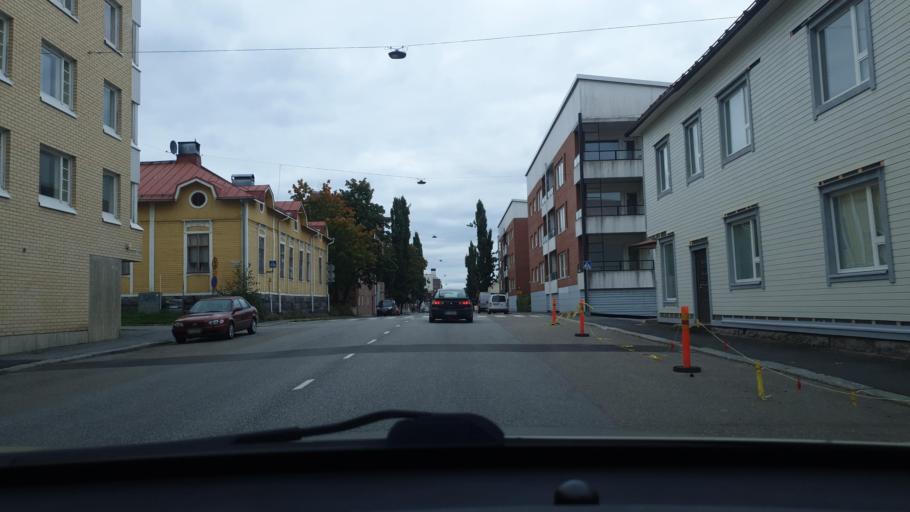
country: FI
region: Ostrobothnia
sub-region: Vaasa
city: Vaasa
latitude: 63.0906
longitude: 21.6270
